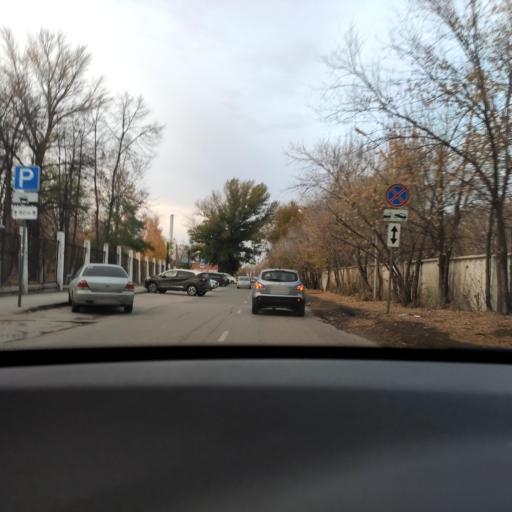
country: RU
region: Samara
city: Samara
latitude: 53.2062
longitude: 50.1702
